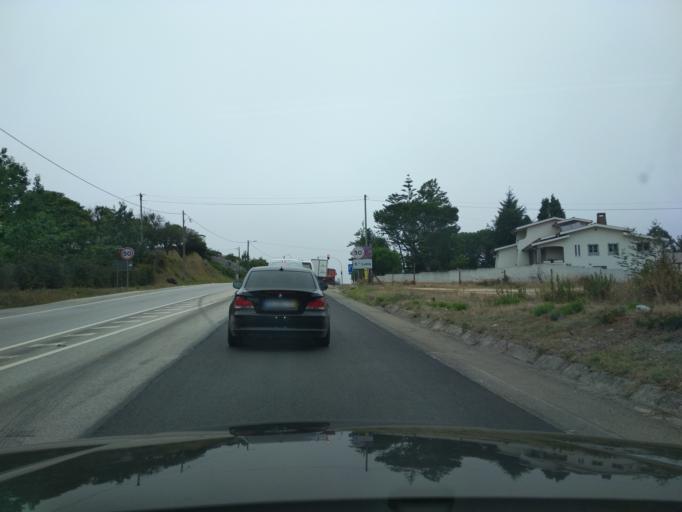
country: PT
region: Aveiro
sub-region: Mealhada
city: Pampilhosa do Botao
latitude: 40.3037
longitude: -8.4478
